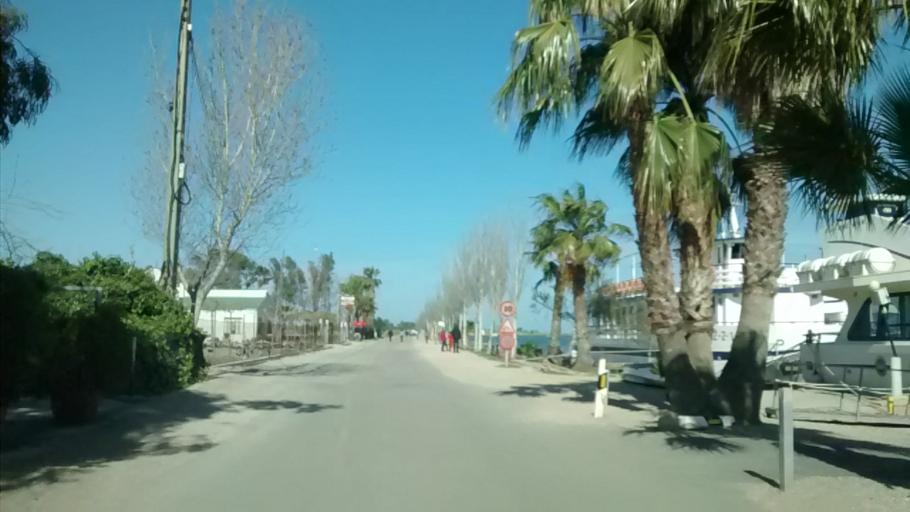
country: ES
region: Catalonia
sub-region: Provincia de Tarragona
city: Deltebre
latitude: 40.7133
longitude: 0.8353
